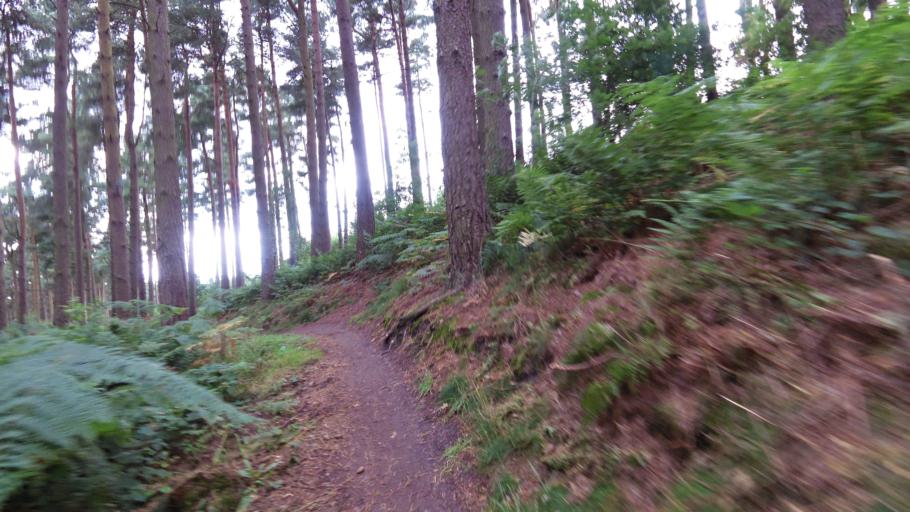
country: GB
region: England
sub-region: North Yorkshire
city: Thornton Dale
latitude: 54.2843
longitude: -0.6846
